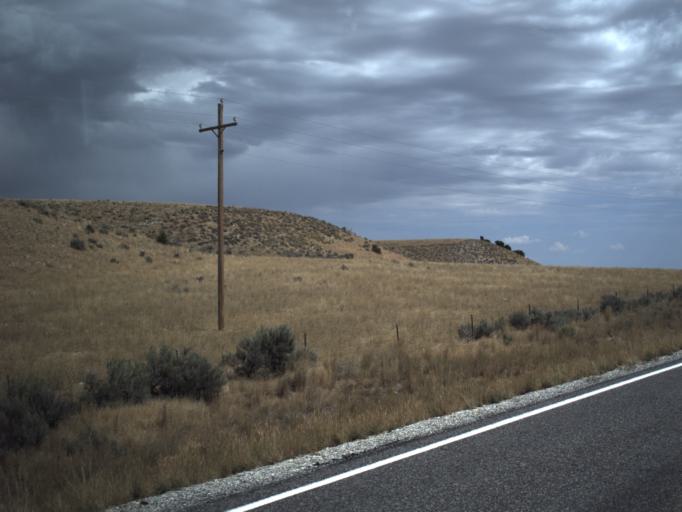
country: US
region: Idaho
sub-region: Cassia County
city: Burley
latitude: 41.8152
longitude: -113.2209
